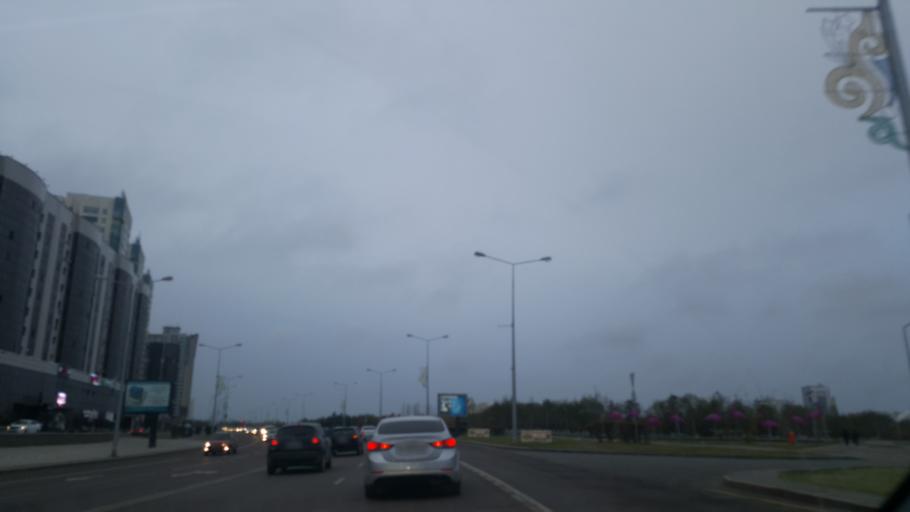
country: KZ
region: Astana Qalasy
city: Astana
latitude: 51.1344
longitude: 71.4603
